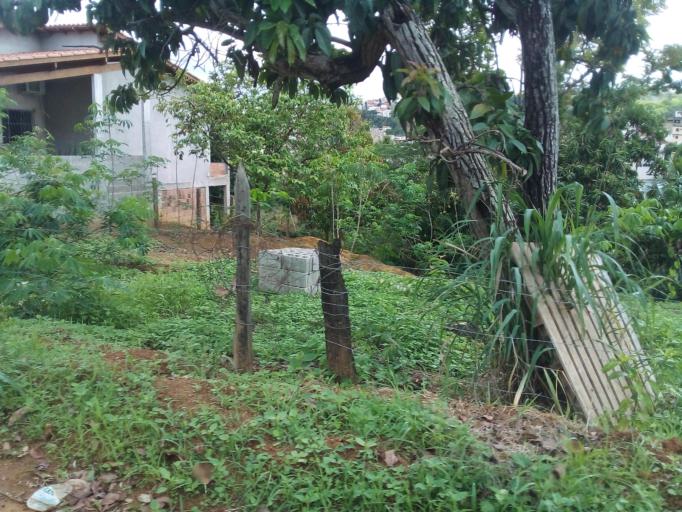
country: BR
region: Espirito Santo
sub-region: Colatina
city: Colatina
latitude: -19.5548
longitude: -40.6380
